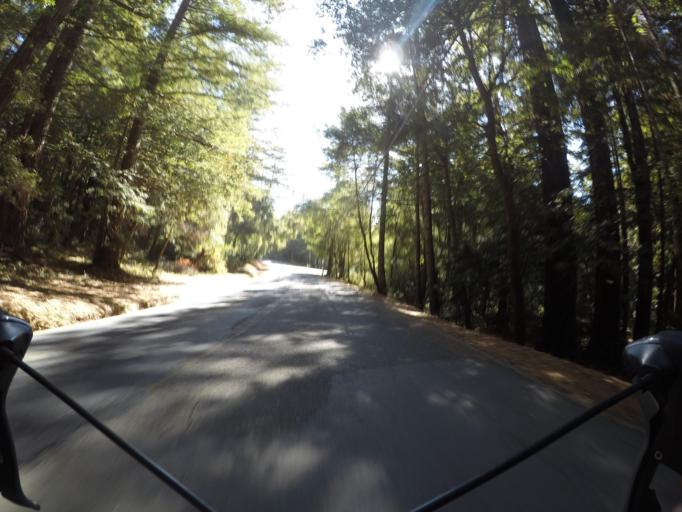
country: US
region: California
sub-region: San Mateo County
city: Portola Valley
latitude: 37.2769
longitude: -122.2922
